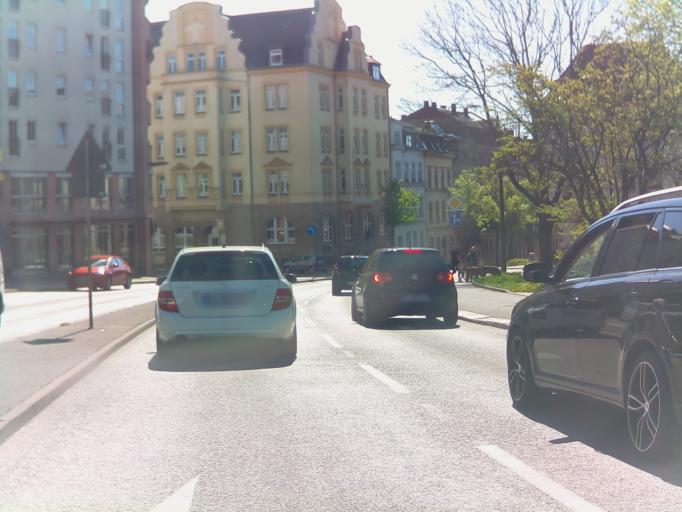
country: DE
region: Saxony
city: Plauen
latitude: 50.5053
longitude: 12.1407
